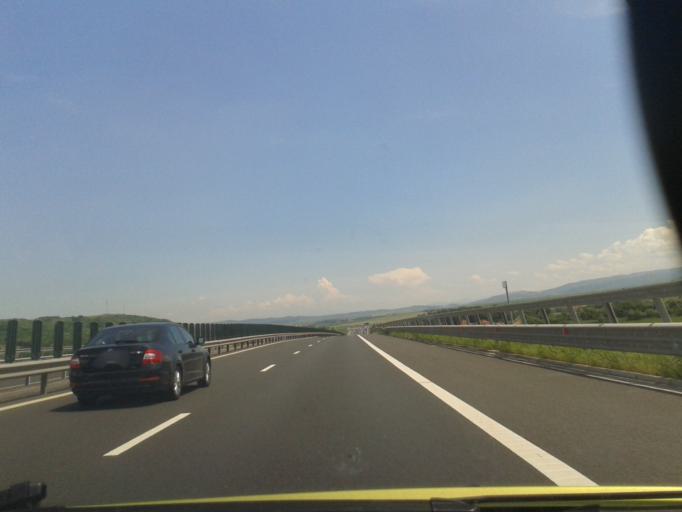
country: RO
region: Alba
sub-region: Comuna Garbova
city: Garbova
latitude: 45.9147
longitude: 23.7313
